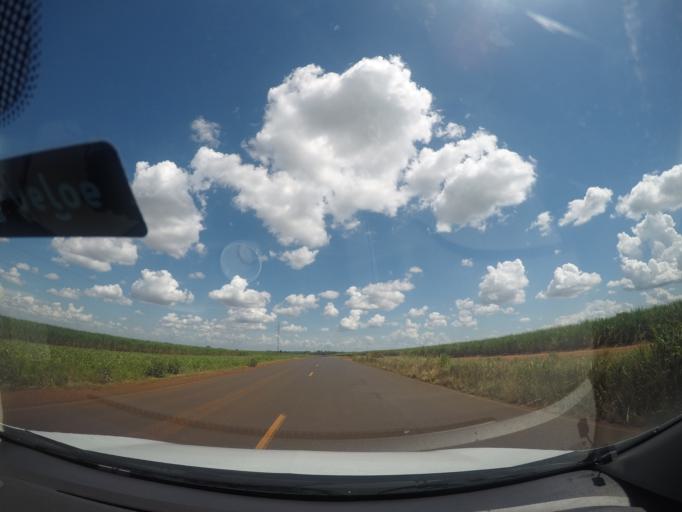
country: BR
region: Minas Gerais
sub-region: Frutal
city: Frutal
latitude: -19.8265
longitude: -48.7333
